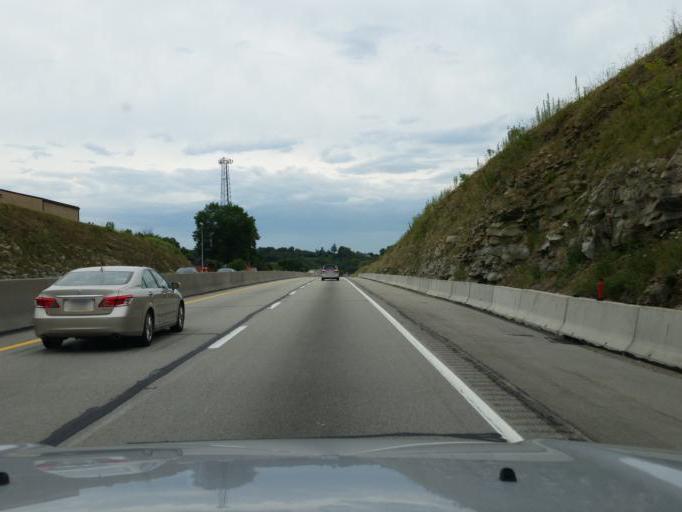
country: US
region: Pennsylvania
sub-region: Westmoreland County
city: Manor
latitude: 40.3680
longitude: -79.6788
